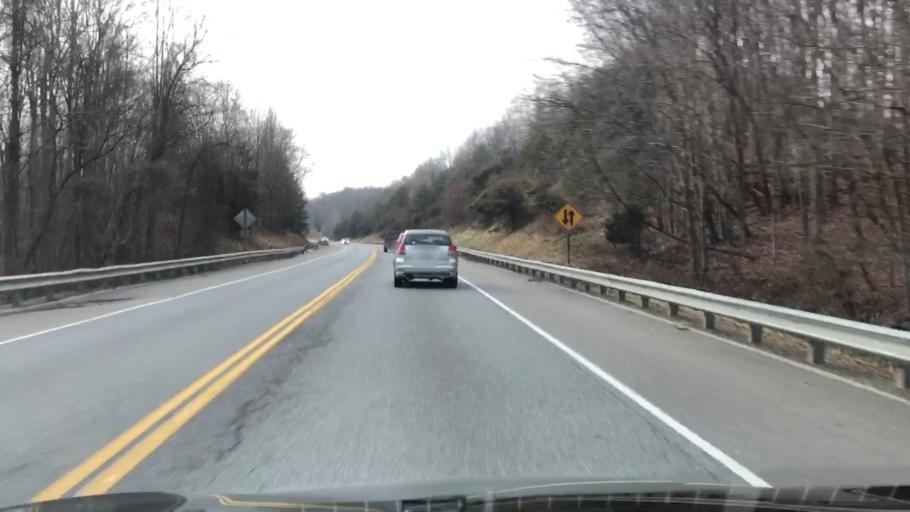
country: US
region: Virginia
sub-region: City of Lynchburg
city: West Lynchburg
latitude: 37.4373
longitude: -79.2351
